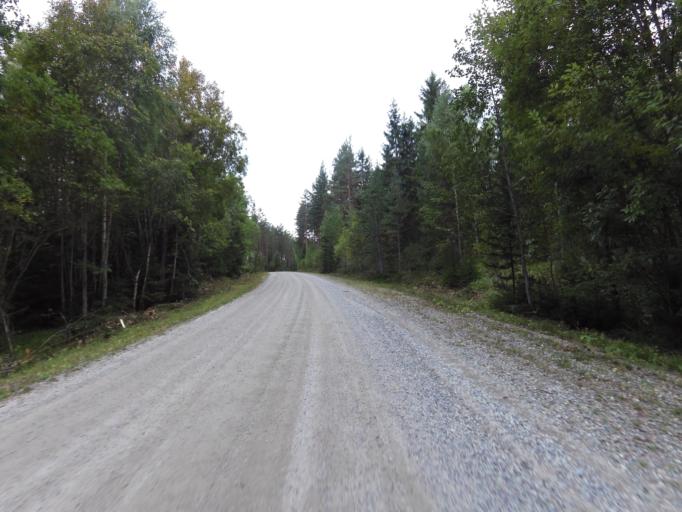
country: SE
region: Gaevleborg
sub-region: Sandvikens Kommun
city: Sandviken
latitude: 60.7598
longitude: 16.8646
